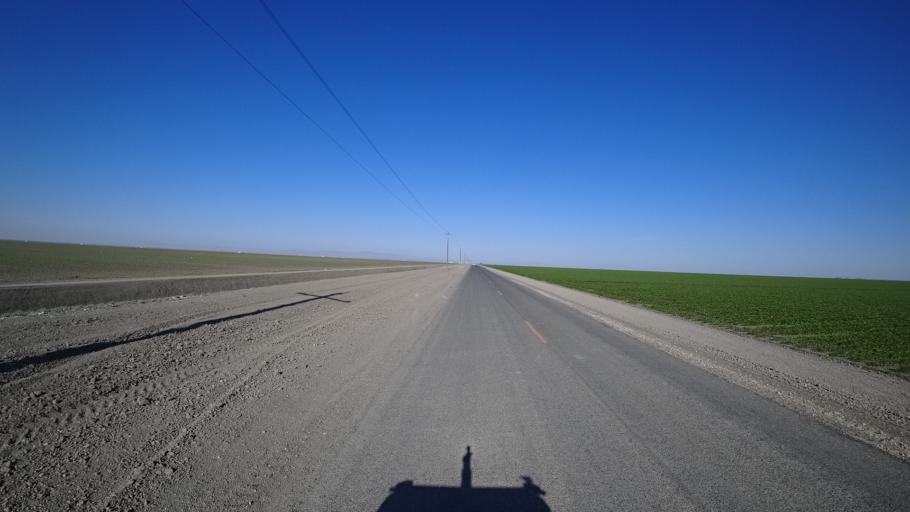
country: US
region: California
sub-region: Kings County
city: Stratford
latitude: 36.0797
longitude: -119.7403
